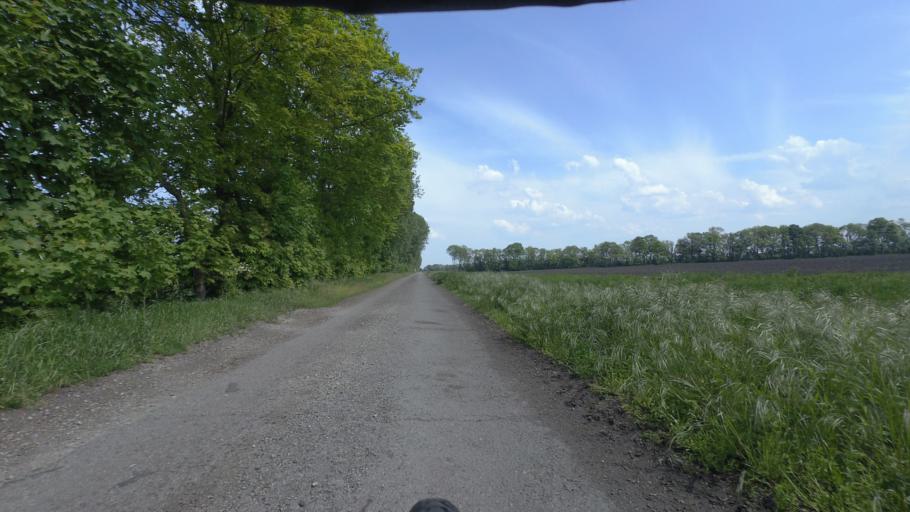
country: DE
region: Lower Saxony
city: Jerxheim
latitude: 52.0621
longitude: 10.8946
